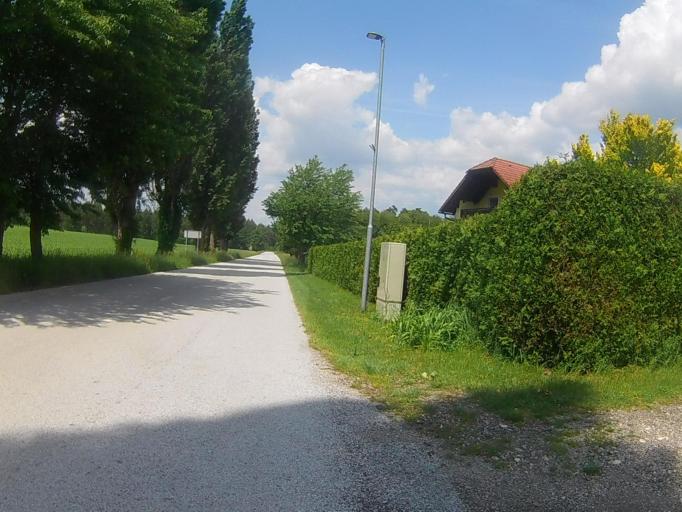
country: SI
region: Kidricevo
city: Kidricevo
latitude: 46.4307
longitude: 15.7799
